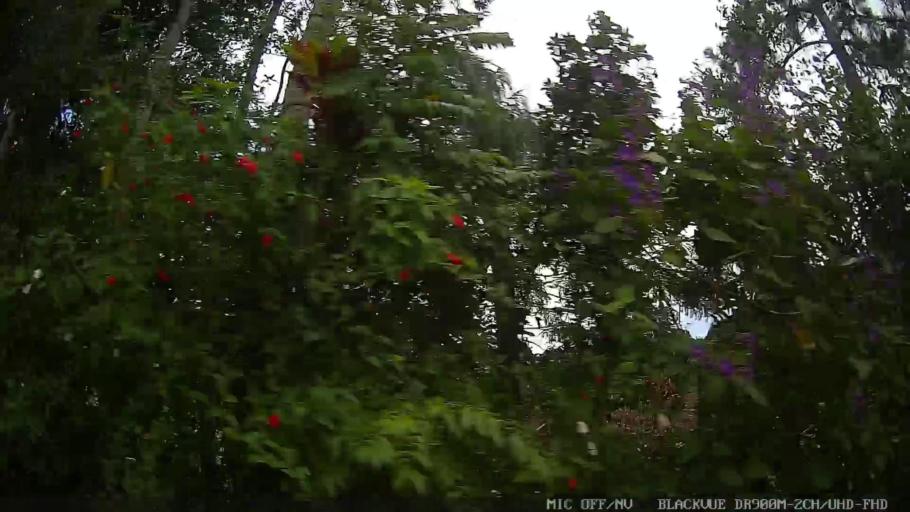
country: BR
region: Sao Paulo
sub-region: Iguape
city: Iguape
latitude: -24.6727
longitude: -47.4478
